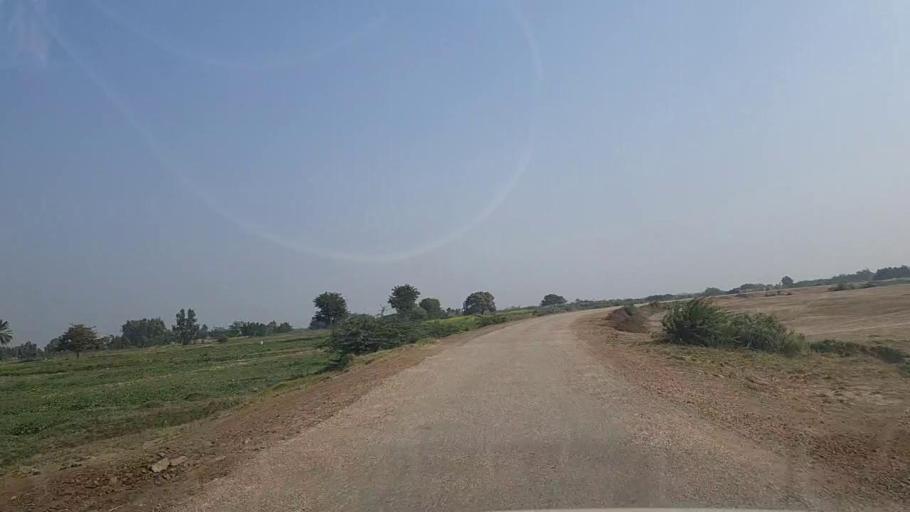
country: PK
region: Sindh
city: Keti Bandar
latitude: 24.2466
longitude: 67.6976
